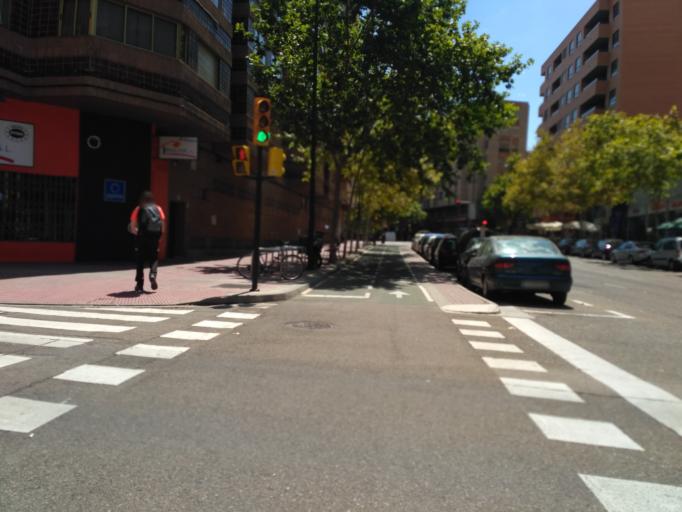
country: ES
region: Aragon
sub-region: Provincia de Zaragoza
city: Delicias
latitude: 41.6544
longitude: -0.9045
